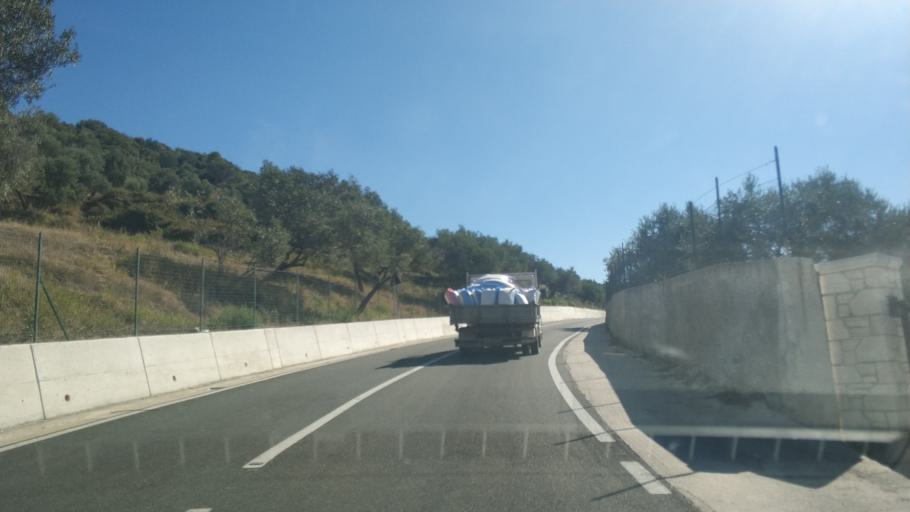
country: AL
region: Vlore
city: Vlore
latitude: 40.4575
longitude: 19.5095
